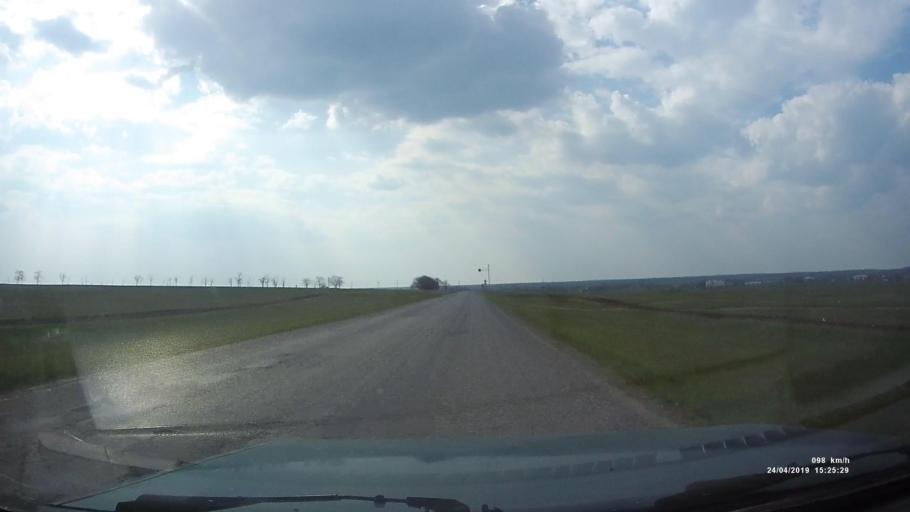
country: RU
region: Rostov
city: Remontnoye
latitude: 46.5526
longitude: 43.0470
